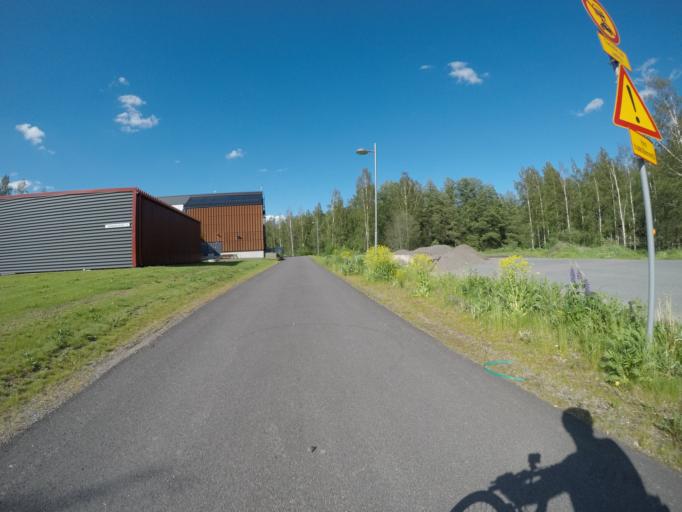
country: FI
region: Haeme
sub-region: Haemeenlinna
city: Haemeenlinna
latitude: 60.9768
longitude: 24.4761
